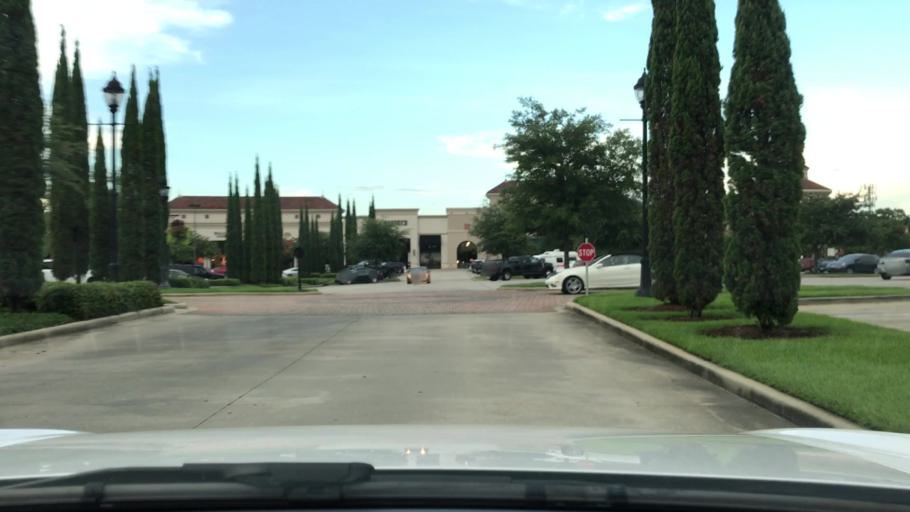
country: US
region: Louisiana
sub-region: East Baton Rouge Parish
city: Westminster
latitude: 30.4318
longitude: -91.1131
